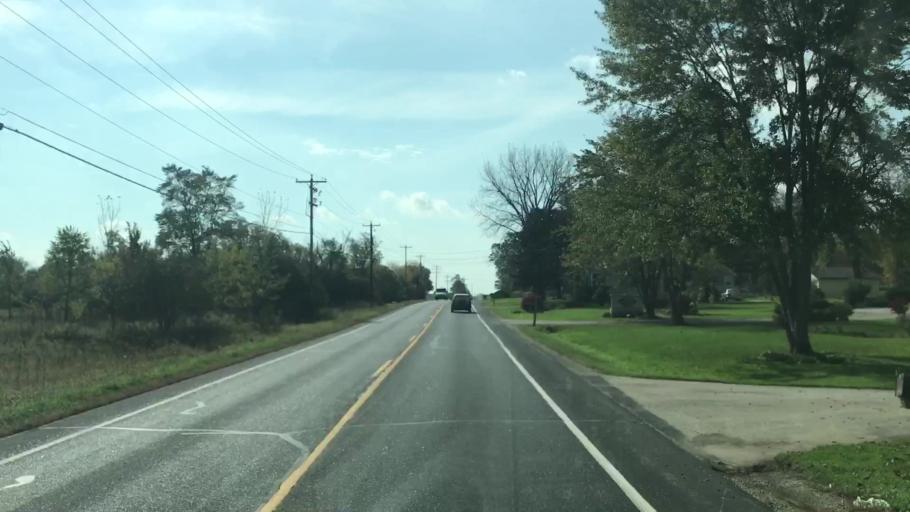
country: US
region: Wisconsin
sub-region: Ozaukee County
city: Mequon
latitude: 43.1967
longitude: -88.0435
